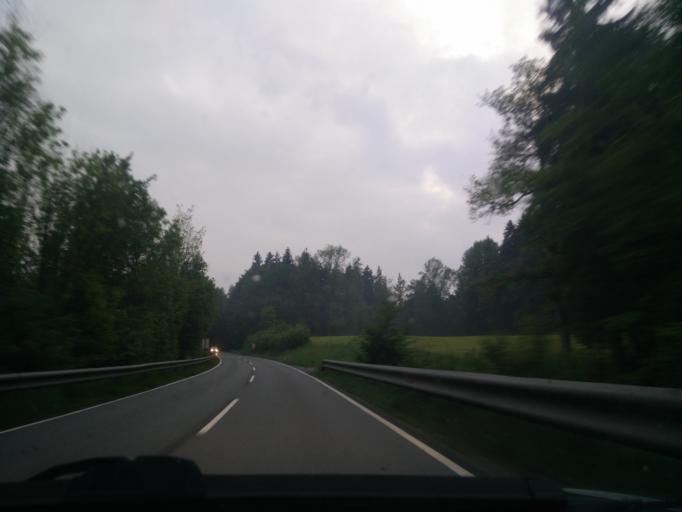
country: AT
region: Salzburg
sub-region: Politischer Bezirk Salzburg-Umgebung
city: Elixhausen
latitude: 47.8514
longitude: 13.0508
